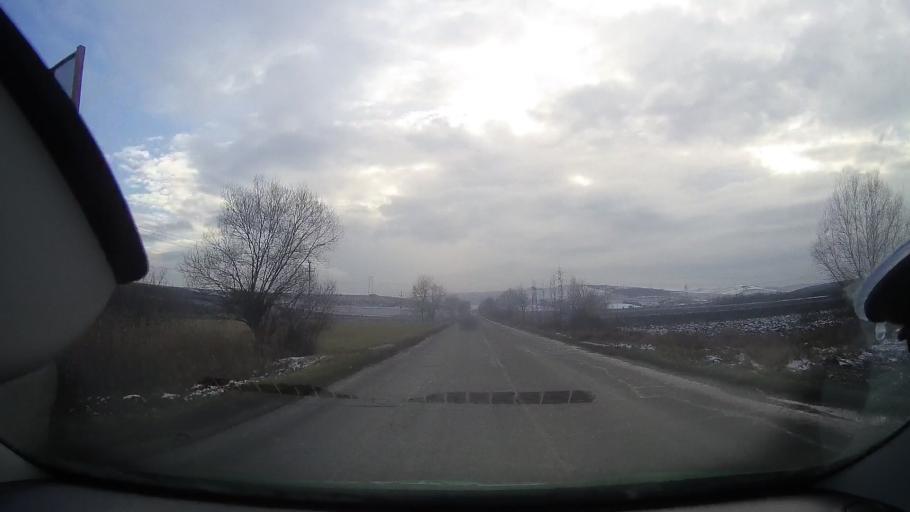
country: RO
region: Mures
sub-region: Comuna Cucerdea
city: Cucerdea
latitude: 46.4254
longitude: 24.2599
